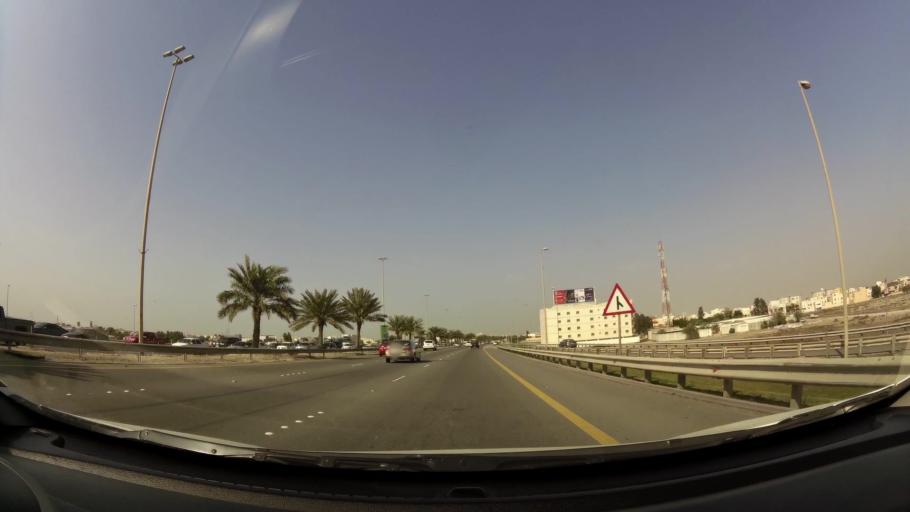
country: BH
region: Northern
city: Madinat `Isa
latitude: 26.1900
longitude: 50.5047
